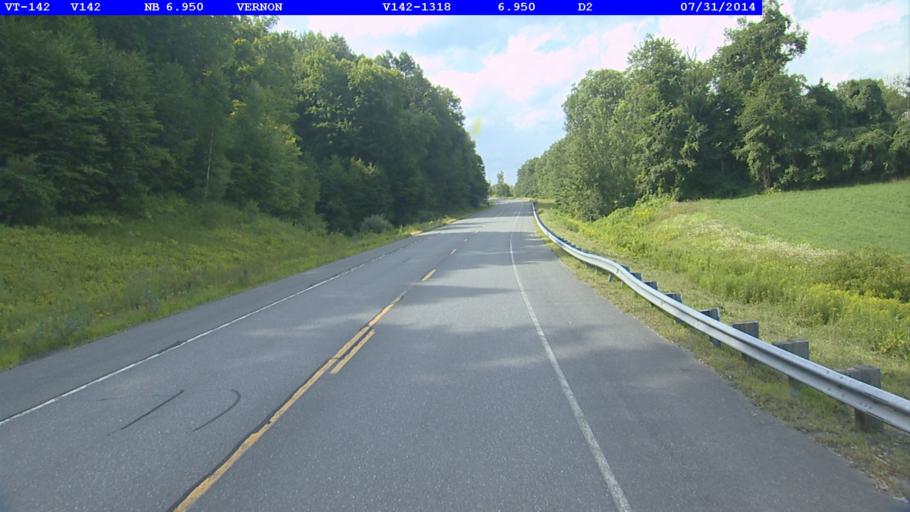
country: US
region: Vermont
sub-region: Windham County
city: Brattleboro
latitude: 42.8014
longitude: -72.5387
